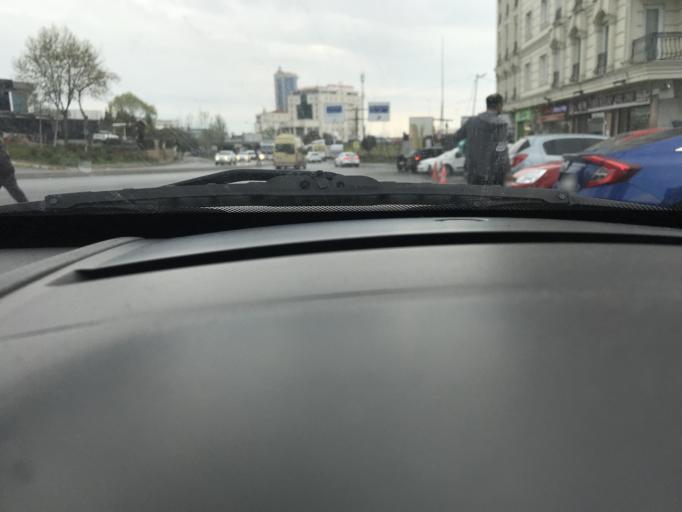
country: TR
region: Istanbul
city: Yakuplu
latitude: 41.0014
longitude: 28.6989
